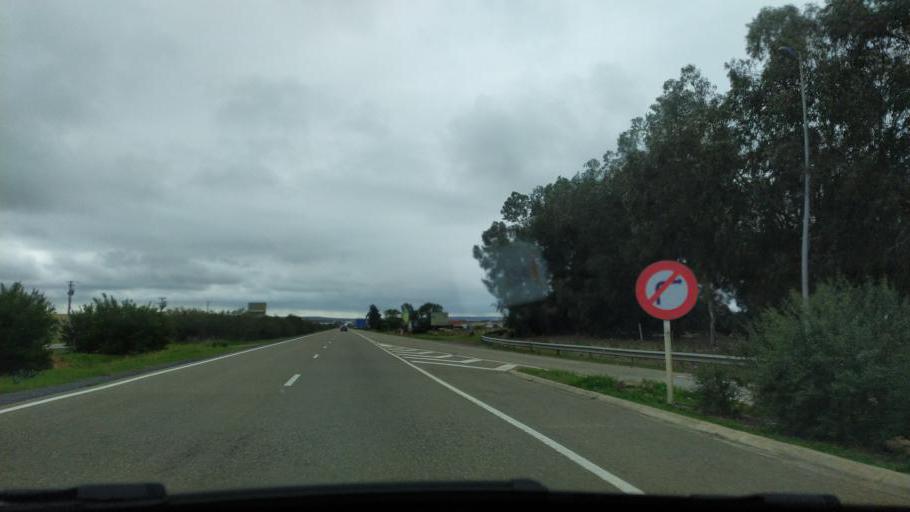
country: MA
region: Gharb-Chrarda-Beni Hssen
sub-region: Kenitra Province
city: Lalla Mimouna
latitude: 34.8747
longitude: -6.2150
